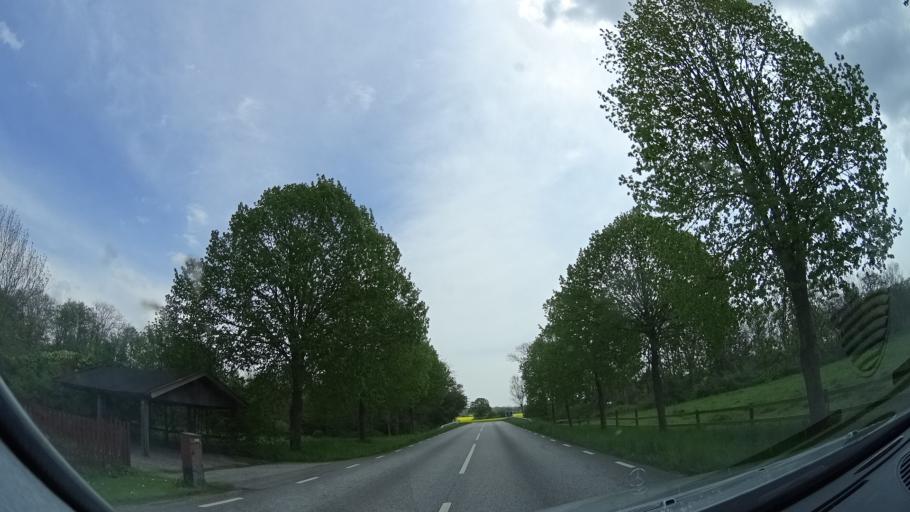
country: SE
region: Skane
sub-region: Hoors Kommun
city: Loberod
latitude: 55.7004
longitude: 13.5820
